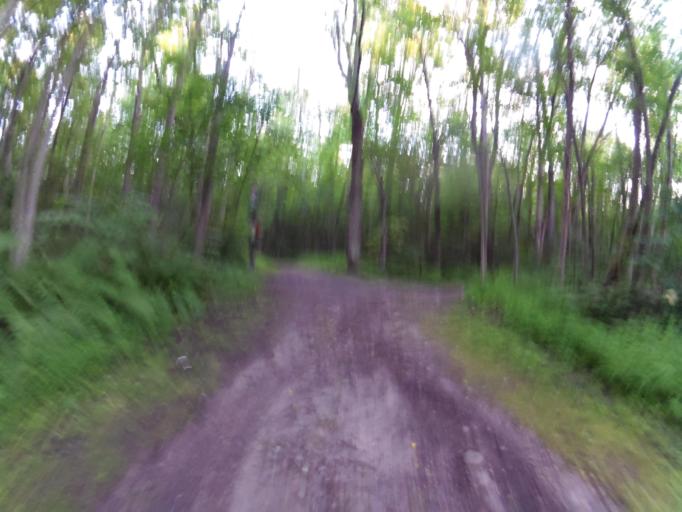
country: CA
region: Ontario
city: Ottawa
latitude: 45.4084
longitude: -75.5757
